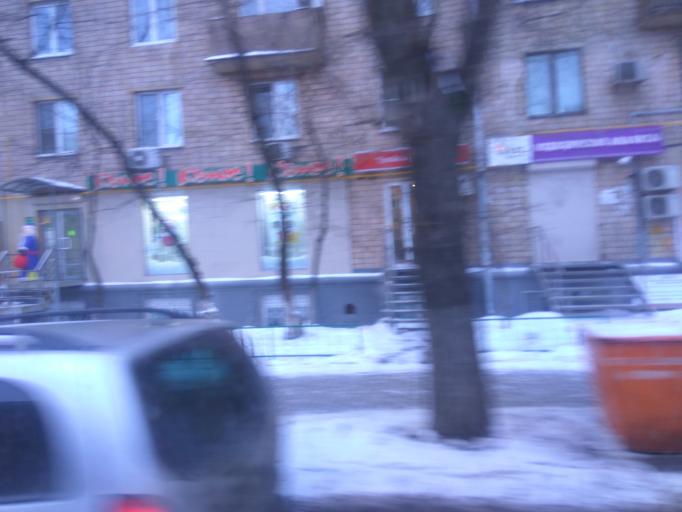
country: RU
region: Moscow
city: Sokol'niki
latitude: 55.7802
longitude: 37.6649
